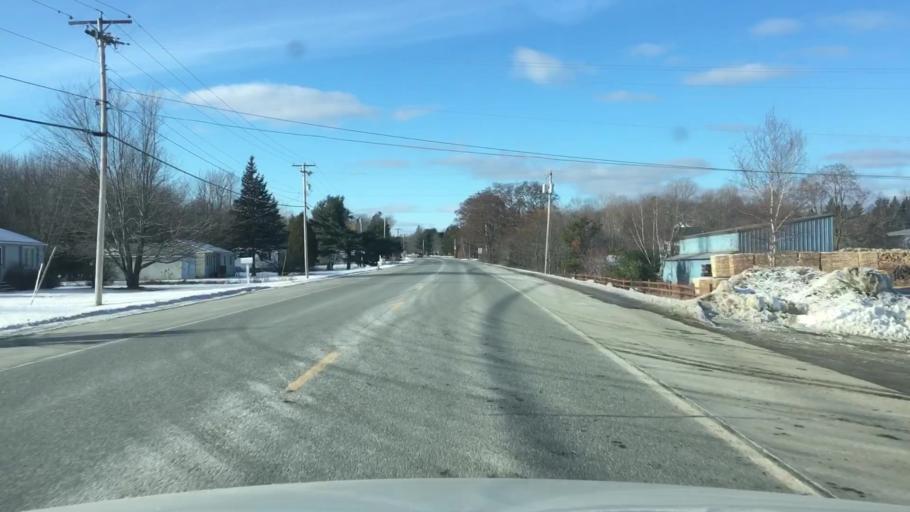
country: US
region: Maine
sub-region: Penobscot County
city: Eddington
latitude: 44.8248
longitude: -68.6537
